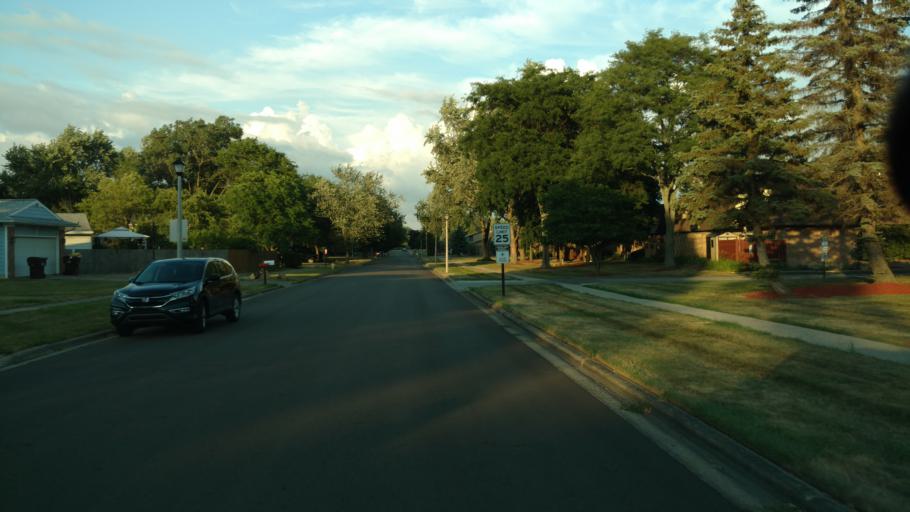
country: US
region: Michigan
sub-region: Eaton County
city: Waverly
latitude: 42.7212
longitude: -84.6159
